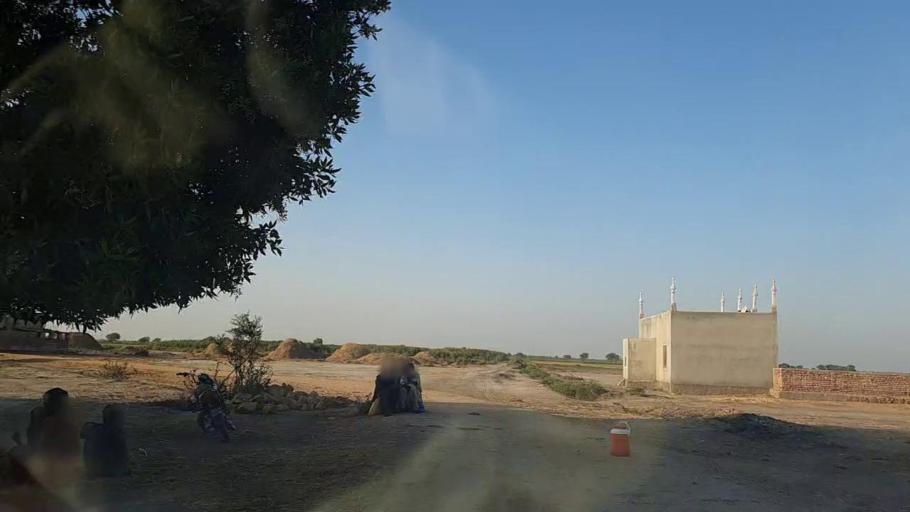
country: PK
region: Sindh
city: Jati
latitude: 24.4190
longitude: 68.1705
